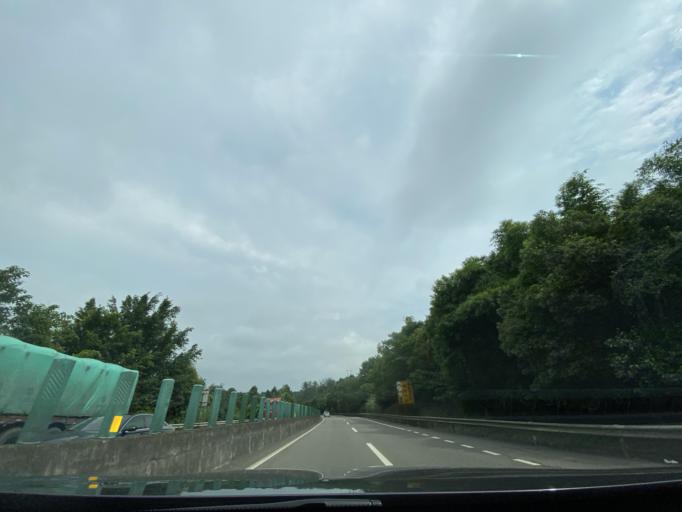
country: CN
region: Sichuan
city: Chonglong
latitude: 29.7262
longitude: 104.9215
